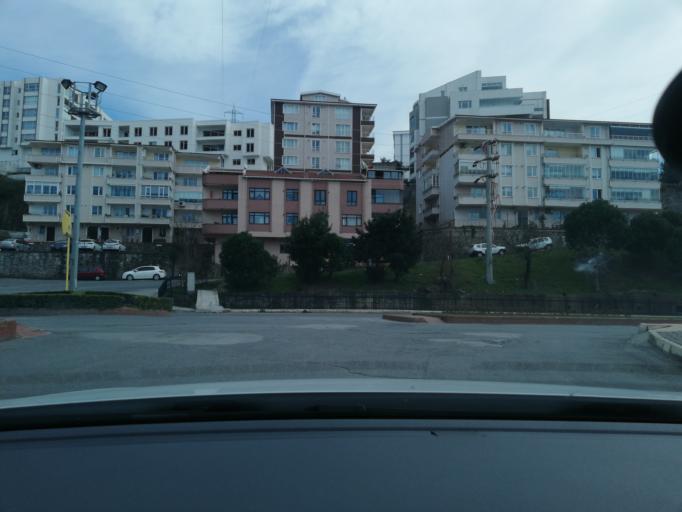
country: TR
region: Zonguldak
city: Eregli
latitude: 41.2931
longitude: 31.4087
